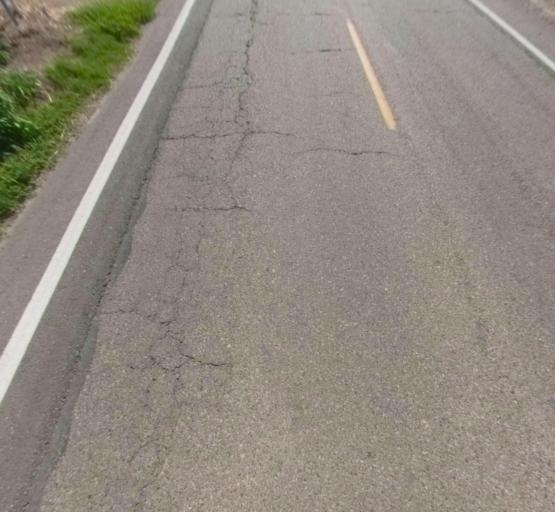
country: US
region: California
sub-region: Madera County
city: Chowchilla
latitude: 37.1127
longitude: -120.3788
